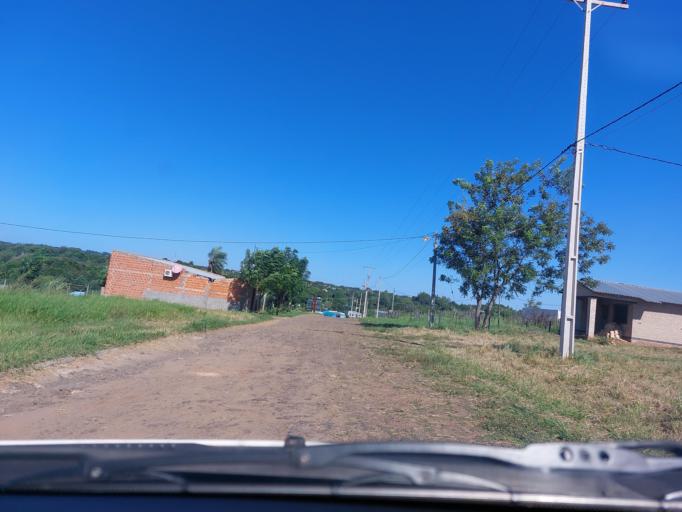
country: PY
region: San Pedro
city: Guayaybi
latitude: -24.6529
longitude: -56.4491
